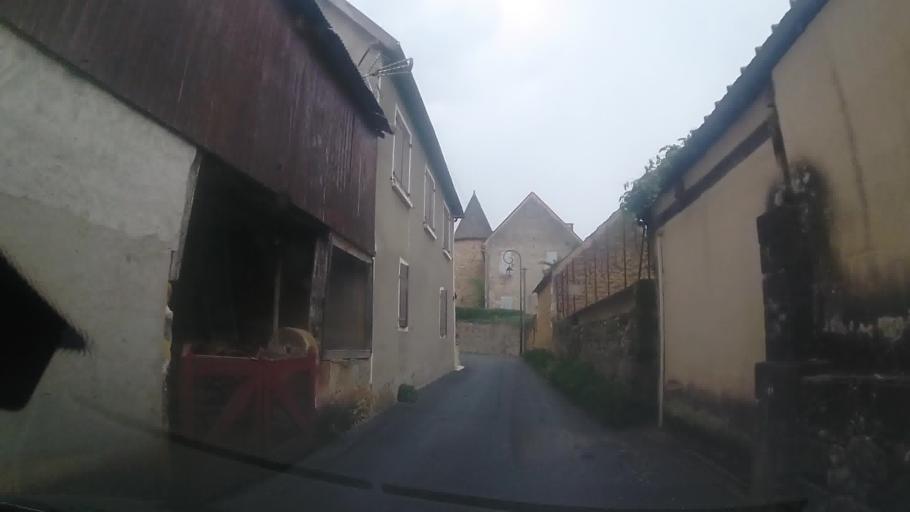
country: FR
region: Aquitaine
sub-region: Departement de la Dordogne
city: Cenac-et-Saint-Julien
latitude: 44.8037
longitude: 1.2031
